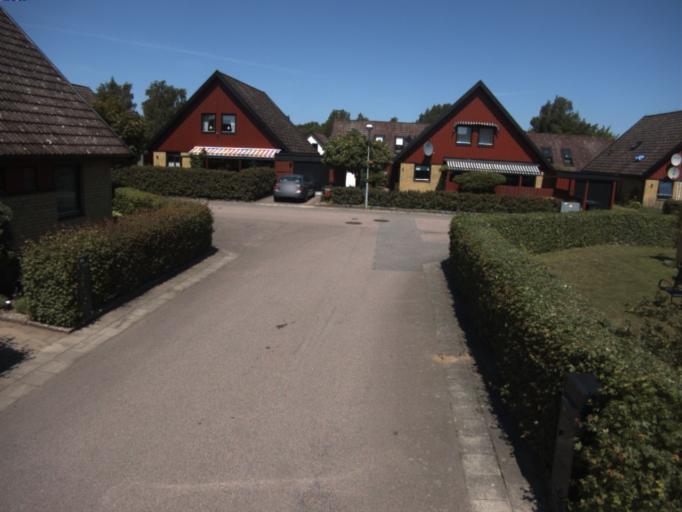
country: SE
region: Skane
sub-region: Helsingborg
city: Rydeback
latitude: 56.0135
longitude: 12.7544
